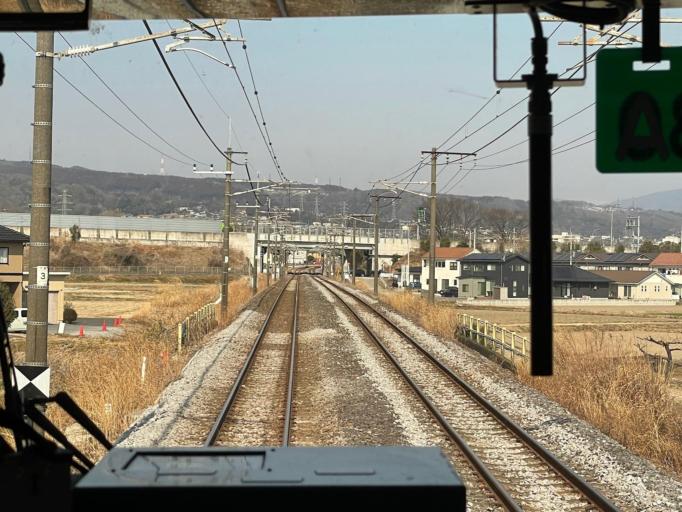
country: JP
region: Gunma
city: Shibukawa
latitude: 36.4701
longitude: 139.0167
